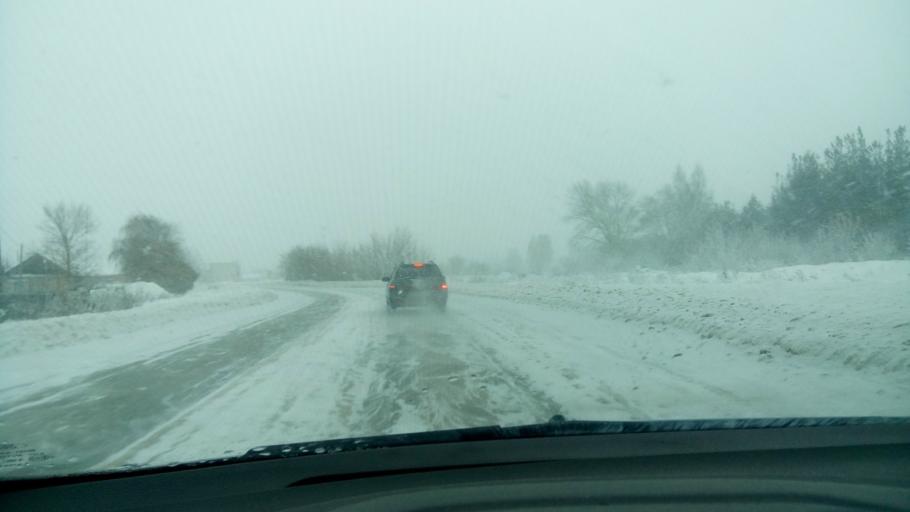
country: RU
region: Sverdlovsk
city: Bogdanovich
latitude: 56.7789
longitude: 62.0151
